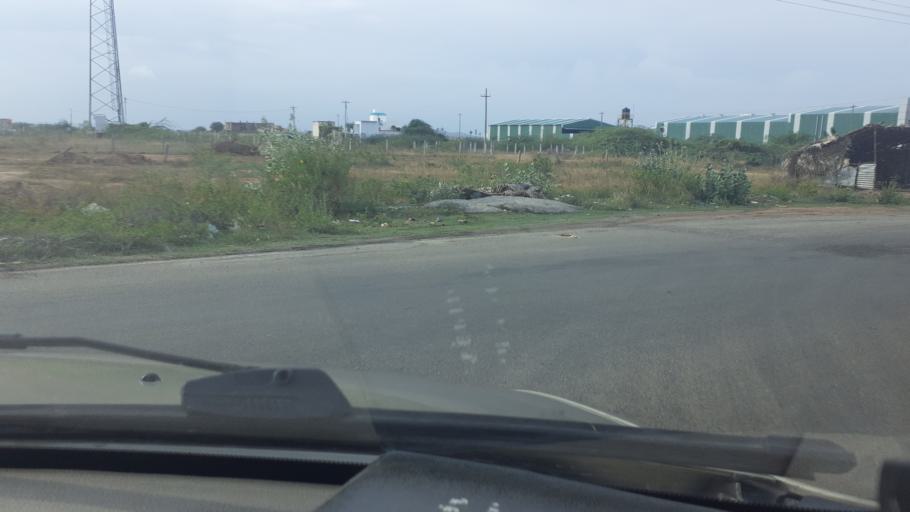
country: IN
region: Tamil Nadu
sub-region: Tirunelveli Kattabo
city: Tirunelveli
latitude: 8.6592
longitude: 77.7144
